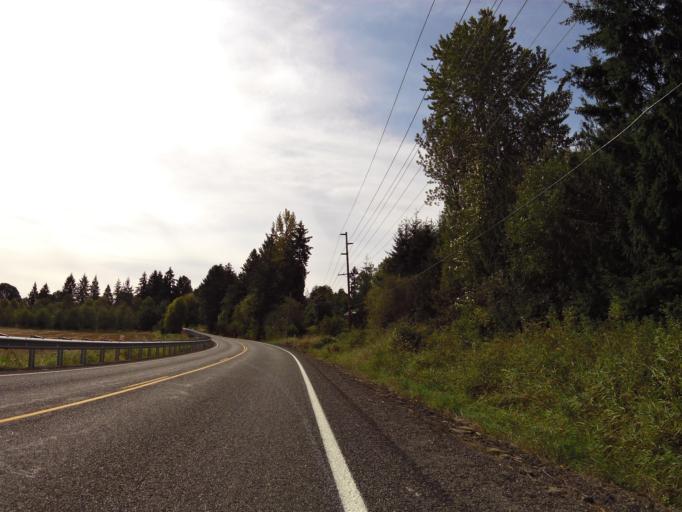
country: US
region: Washington
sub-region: Lewis County
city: Chehalis
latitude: 46.6365
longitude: -122.9714
